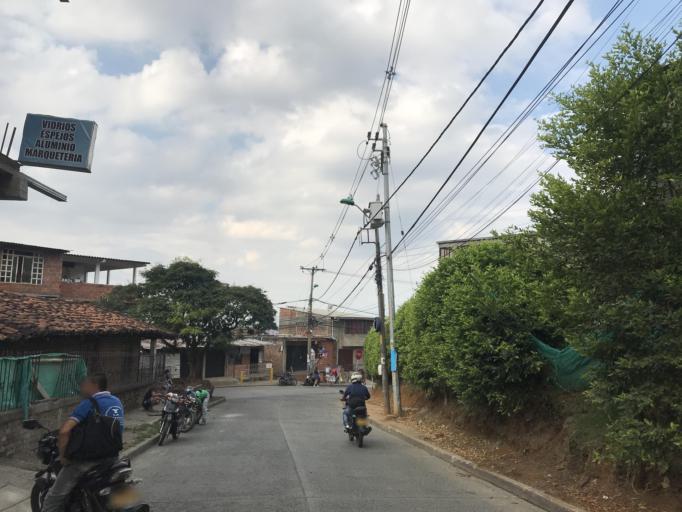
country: CO
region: Valle del Cauca
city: Cali
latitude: 3.3741
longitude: -76.5551
